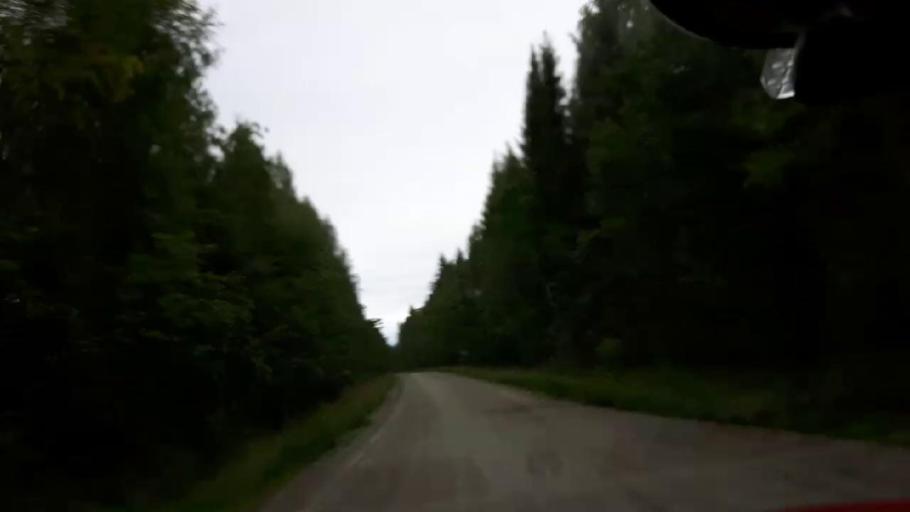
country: SE
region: Vaesternorrland
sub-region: Ange Kommun
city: Ange
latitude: 62.7974
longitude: 15.7705
